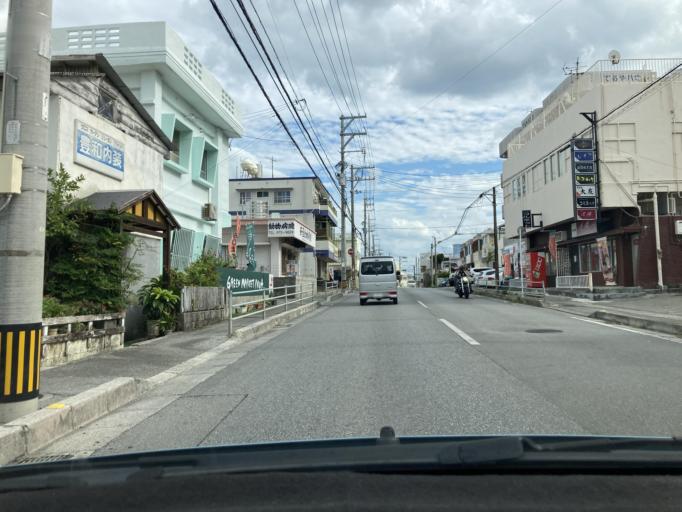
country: JP
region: Okinawa
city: Gushikawa
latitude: 26.3543
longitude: 127.8337
